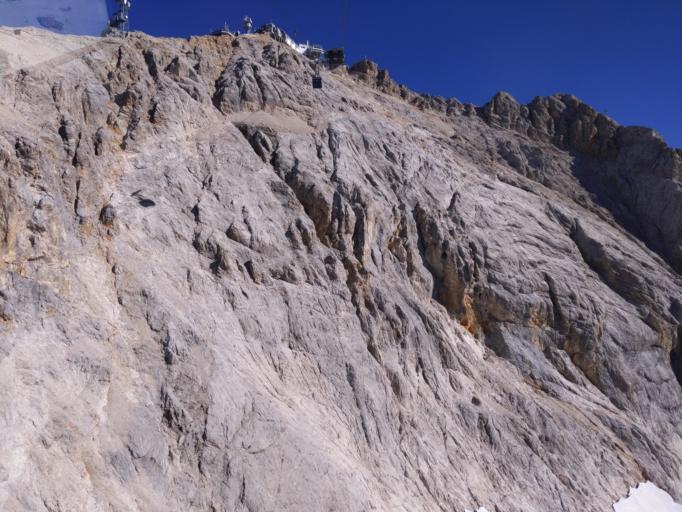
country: AT
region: Tyrol
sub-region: Politischer Bezirk Reutte
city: Ehrwald
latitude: 47.4166
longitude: 10.9823
